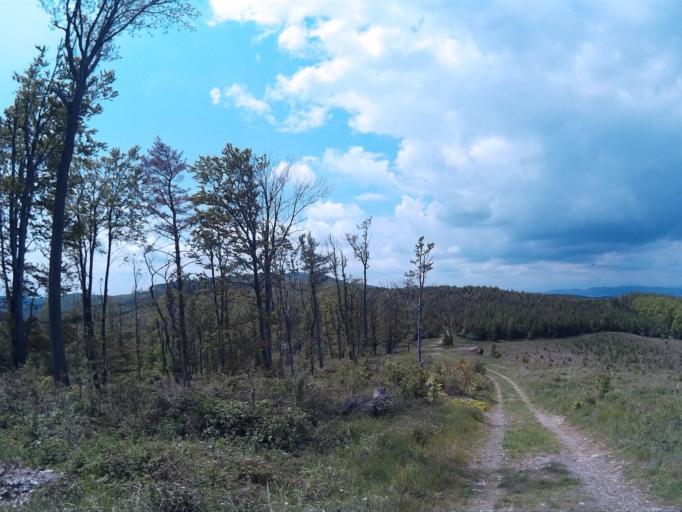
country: AT
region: Burgenland
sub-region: Politischer Bezirk Oberwart
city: Rechnitz
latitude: 47.3628
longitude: 16.4773
